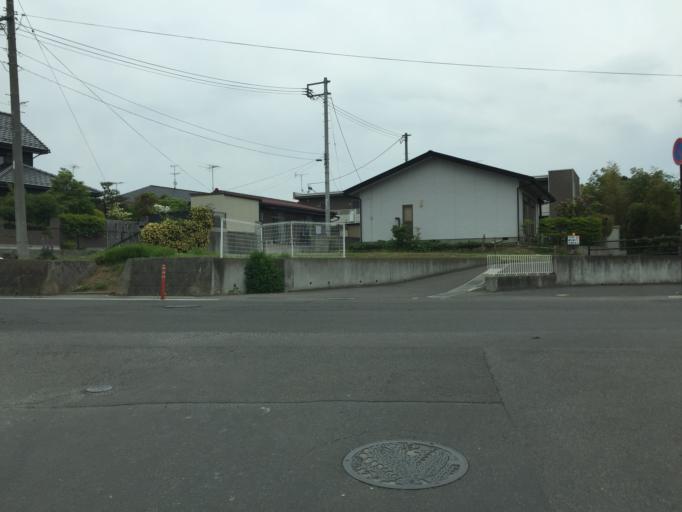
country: JP
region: Fukushima
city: Fukushima-shi
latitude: 37.7834
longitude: 140.4508
